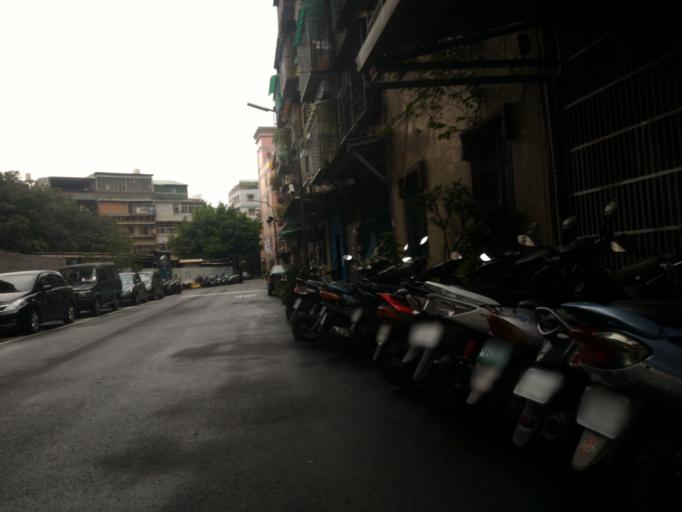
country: TW
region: Taipei
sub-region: Taipei
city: Banqiao
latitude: 25.0415
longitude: 121.4565
